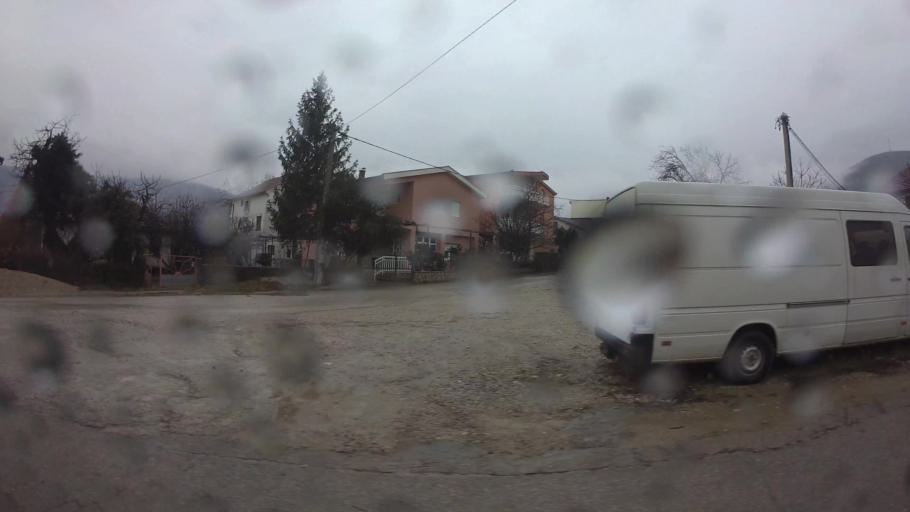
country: BA
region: Federation of Bosnia and Herzegovina
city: Cim
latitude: 43.3495
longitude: 17.7862
